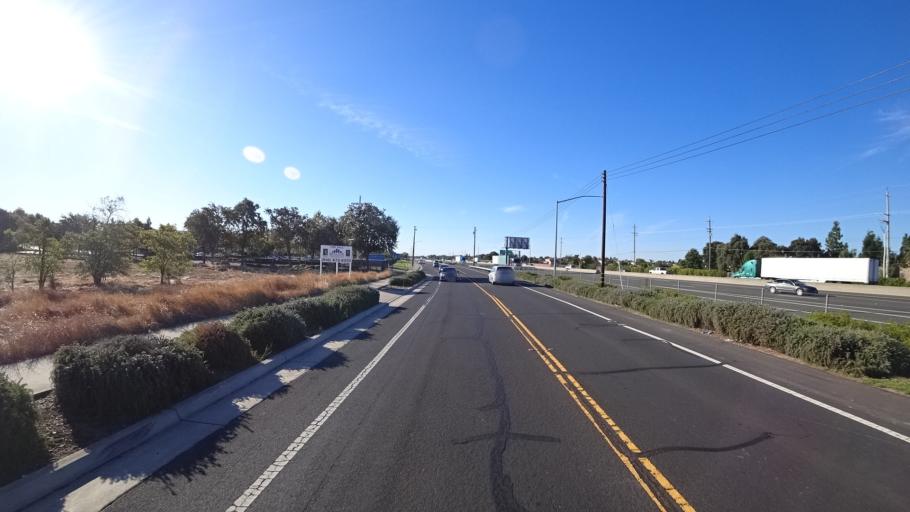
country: US
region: California
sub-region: Sacramento County
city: Laguna
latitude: 38.4336
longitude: -121.3993
